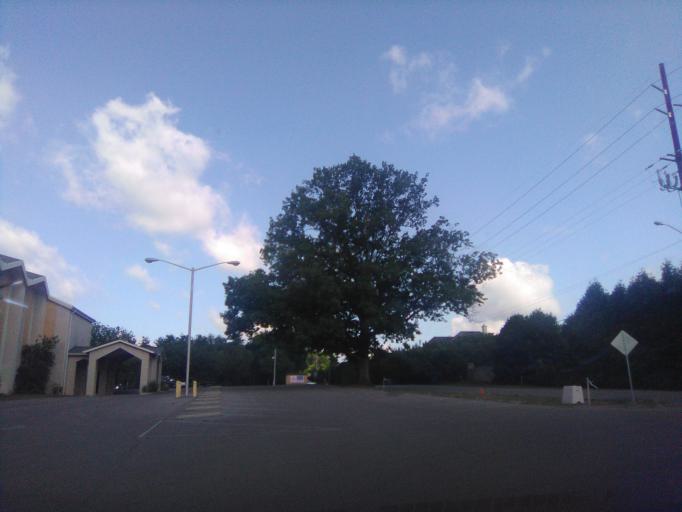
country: US
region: Tennessee
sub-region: Davidson County
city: Belle Meade
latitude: 36.1152
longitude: -86.8636
